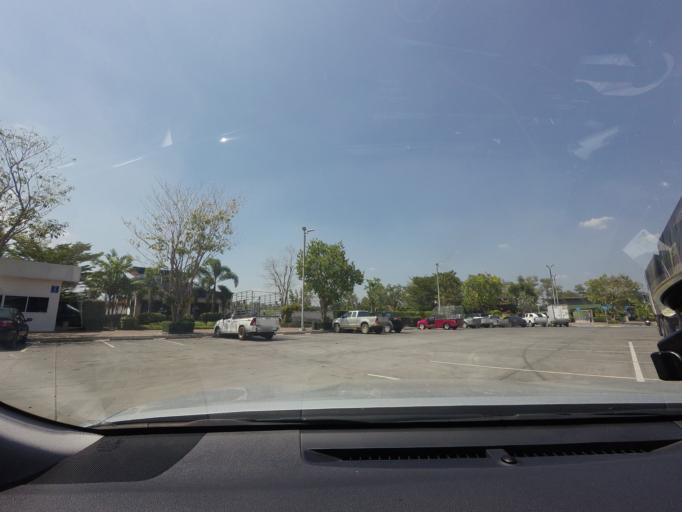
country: TH
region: Chumphon
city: Sawi
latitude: 10.1826
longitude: 99.0961
